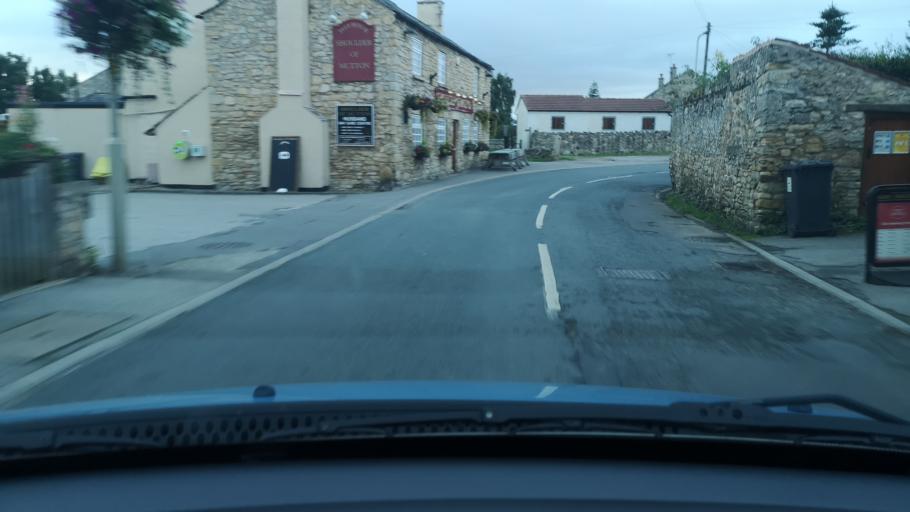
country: GB
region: England
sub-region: Doncaster
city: Norton
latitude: 53.6437
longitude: -1.2163
